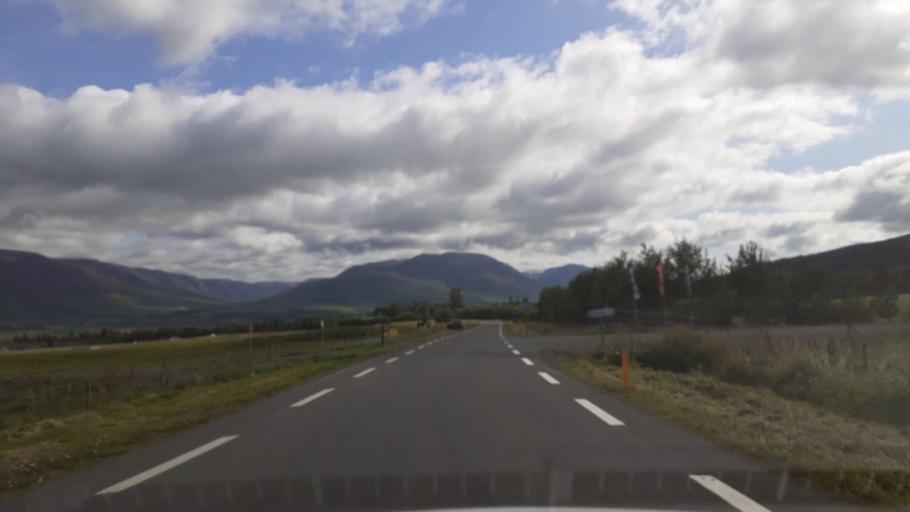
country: IS
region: Northeast
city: Akureyri
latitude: 65.6518
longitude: -18.0929
